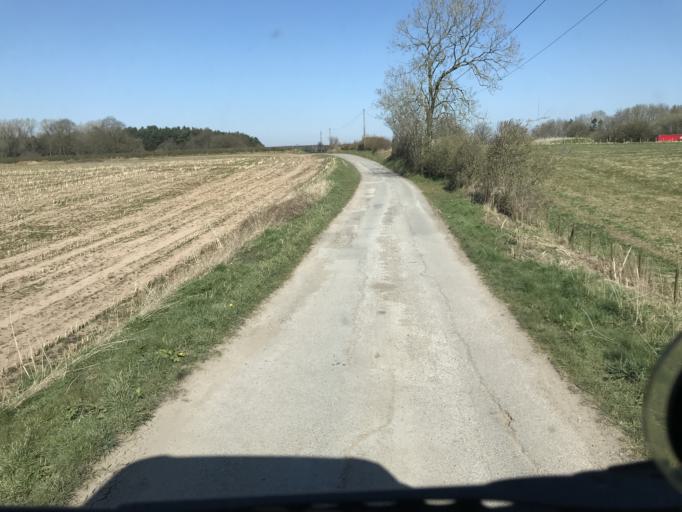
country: GB
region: England
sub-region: Cheshire East
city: Siddington
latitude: 53.2640
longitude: -2.2559
